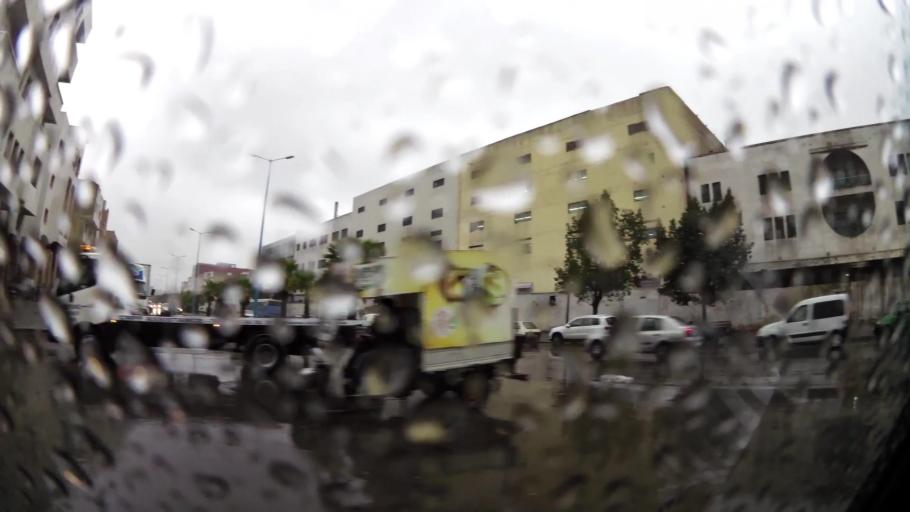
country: MA
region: Grand Casablanca
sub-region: Mediouna
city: Tit Mellil
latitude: 33.5679
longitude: -7.5258
